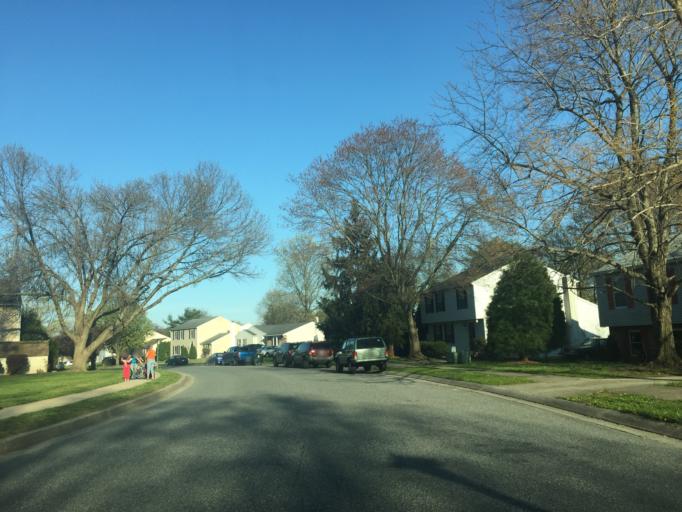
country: US
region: Maryland
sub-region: Harford County
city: Riverside
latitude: 39.4755
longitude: -76.2440
